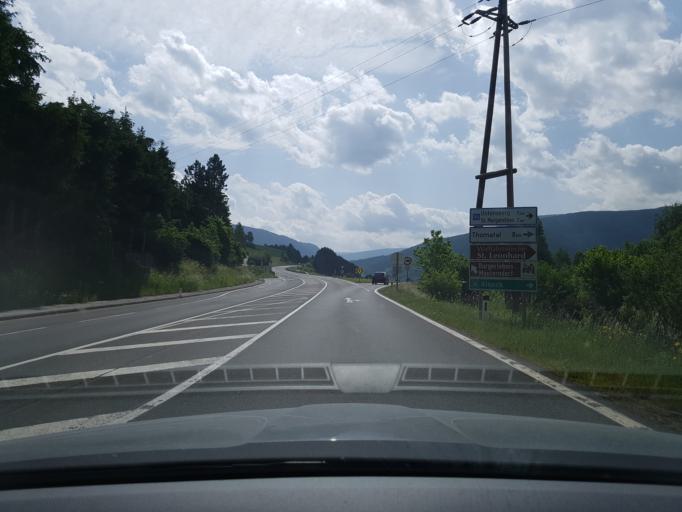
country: AT
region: Salzburg
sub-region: Politischer Bezirk Tamsweg
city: Sankt Margarethen im Lungau
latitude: 47.0934
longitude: 13.6771
